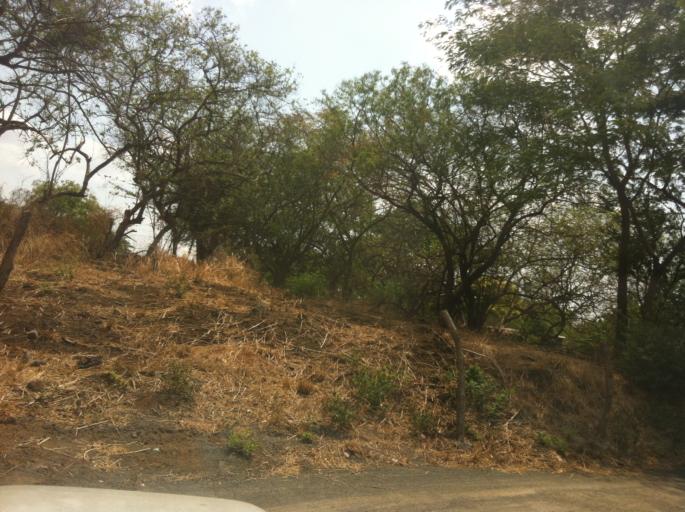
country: NI
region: Managua
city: Ciudad Sandino
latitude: 12.0833
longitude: -86.3315
